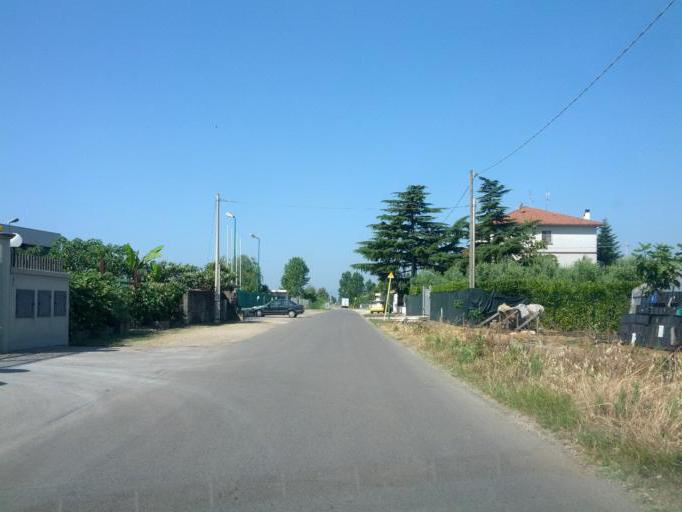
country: IT
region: Latium
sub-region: Provincia di Latina
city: Fondi
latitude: 41.3363
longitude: 13.4223
